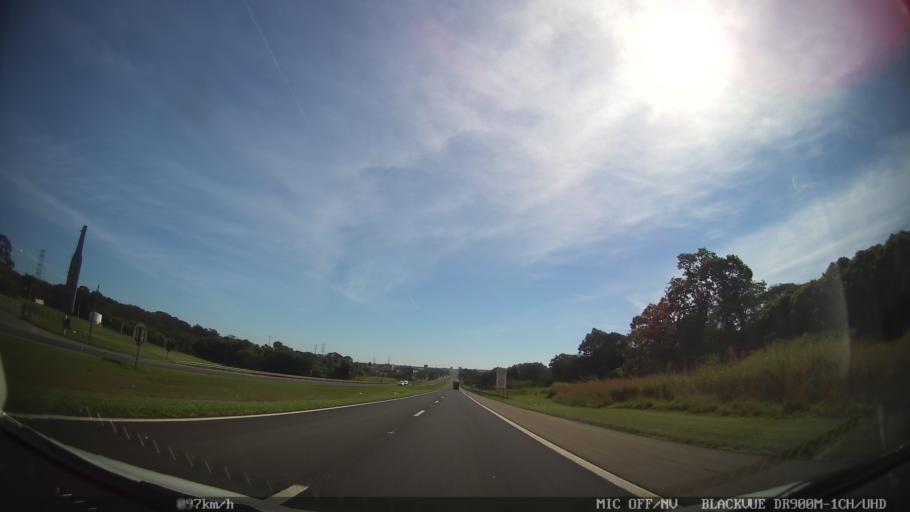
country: BR
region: Sao Paulo
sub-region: Pirassununga
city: Pirassununga
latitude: -22.0076
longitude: -47.4425
